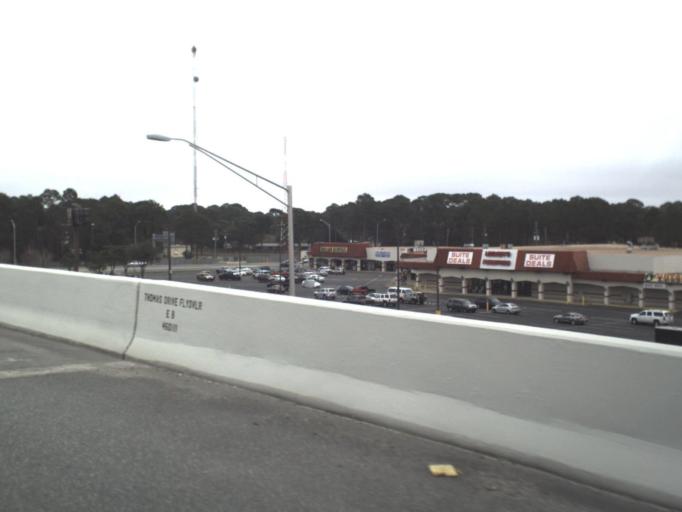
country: US
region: Florida
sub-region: Bay County
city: Upper Grand Lagoon
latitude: 30.1880
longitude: -85.7639
